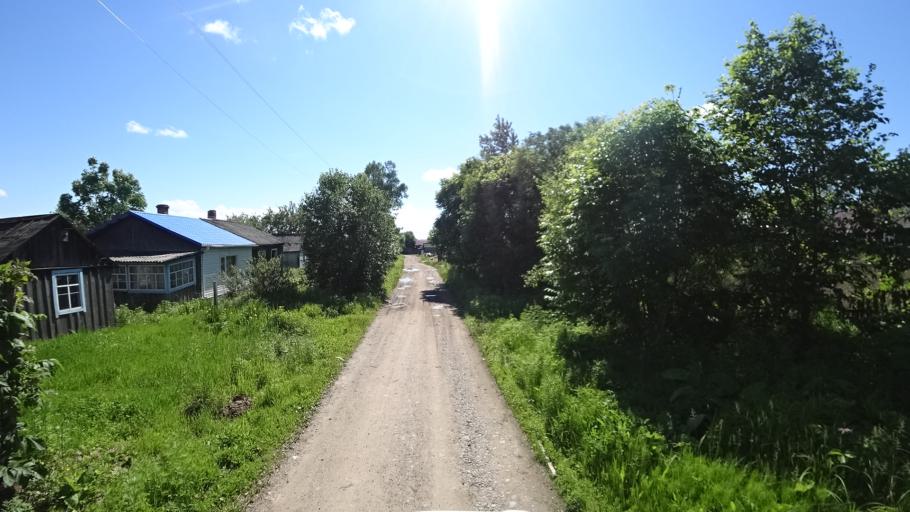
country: RU
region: Khabarovsk Krai
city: Khor
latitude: 47.8863
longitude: 135.0345
